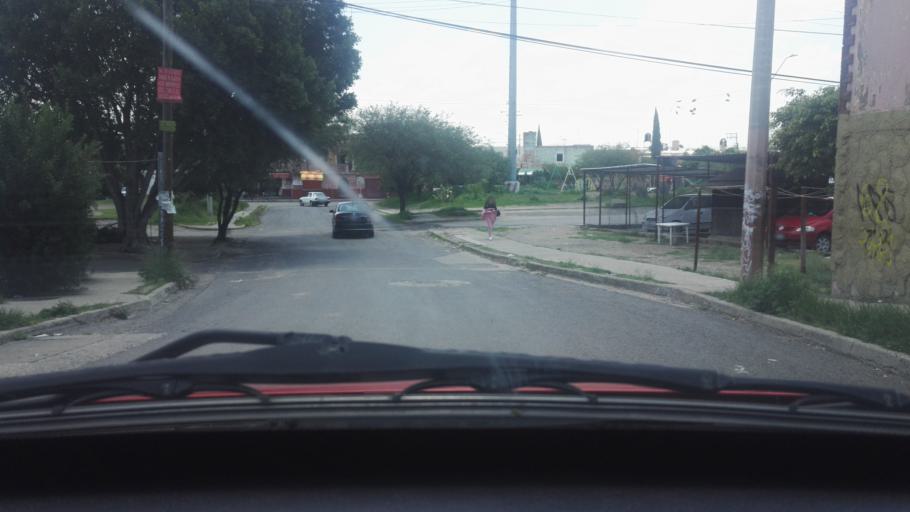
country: MX
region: Guanajuato
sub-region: Leon
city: San Jose de Duran (Los Troncoso)
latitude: 21.0875
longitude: -101.6293
